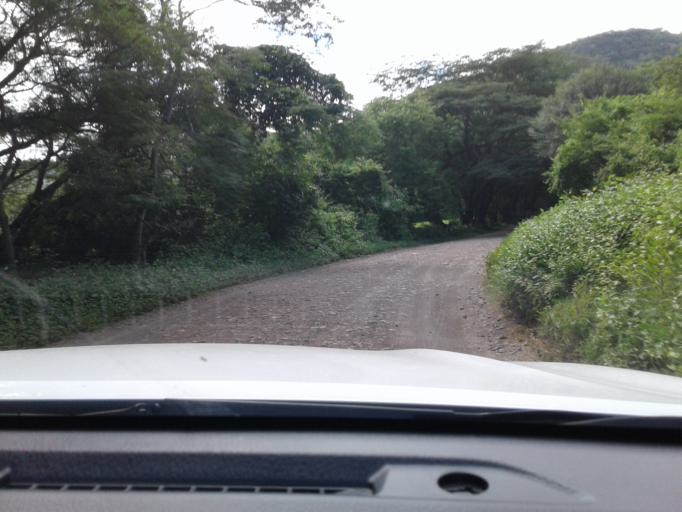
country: NI
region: Matagalpa
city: Ciudad Dario
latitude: 12.8454
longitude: -86.0600
